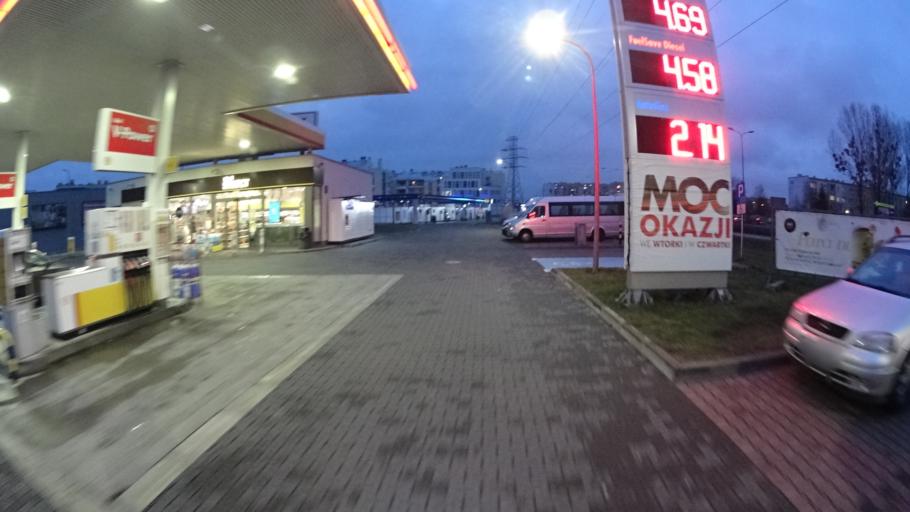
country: PL
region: Masovian Voivodeship
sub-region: Warszawa
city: Bemowo
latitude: 52.2305
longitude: 20.8964
